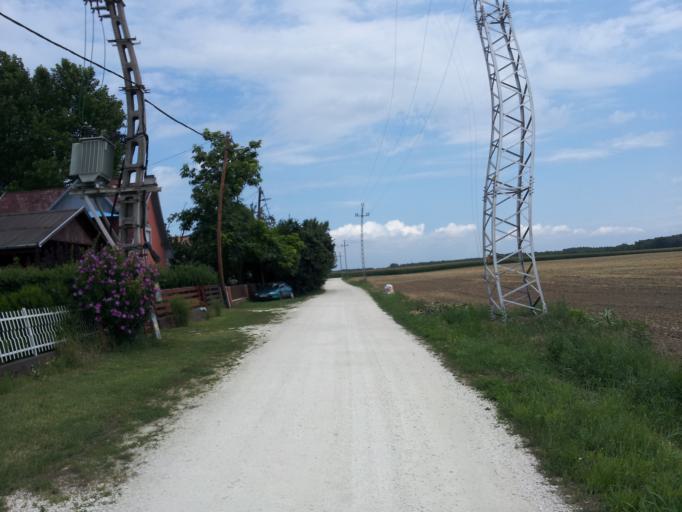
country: HU
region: Pest
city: Szigetcsep
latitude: 47.2327
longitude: 18.9743
